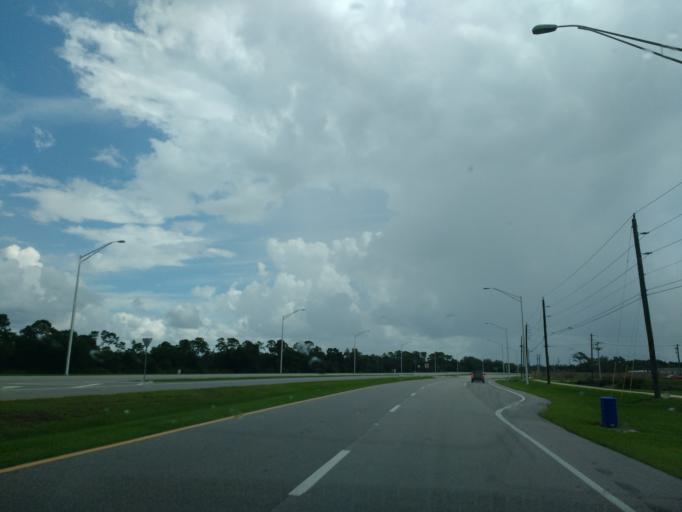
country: US
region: Florida
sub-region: Lee County
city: Burnt Store Marina
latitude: 26.7984
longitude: -82.0373
